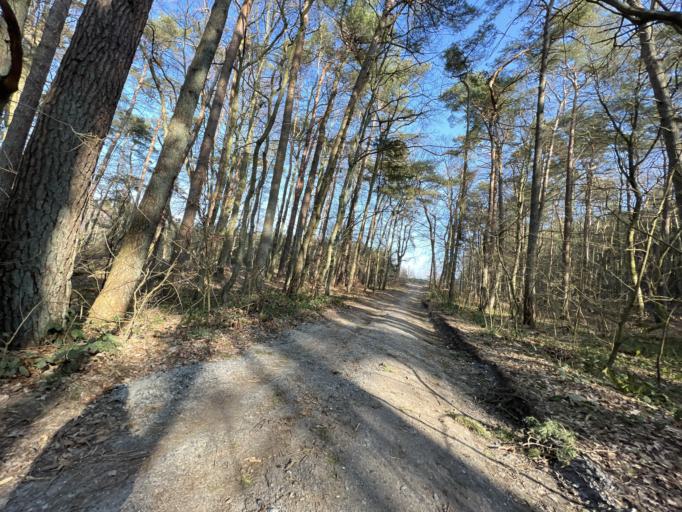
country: DE
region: Mecklenburg-Vorpommern
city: Sagard
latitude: 54.4814
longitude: 13.5627
